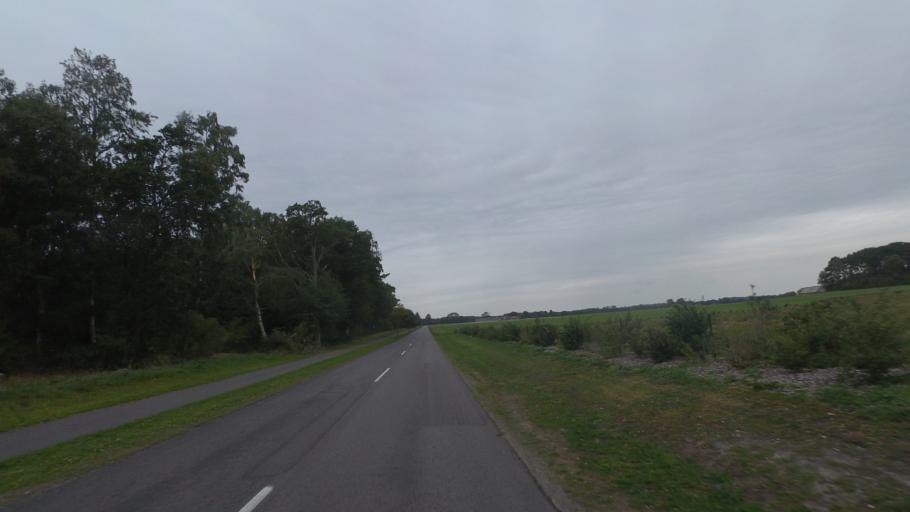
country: DK
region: Capital Region
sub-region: Bornholm Kommune
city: Akirkeby
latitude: 55.0027
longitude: 15.0186
